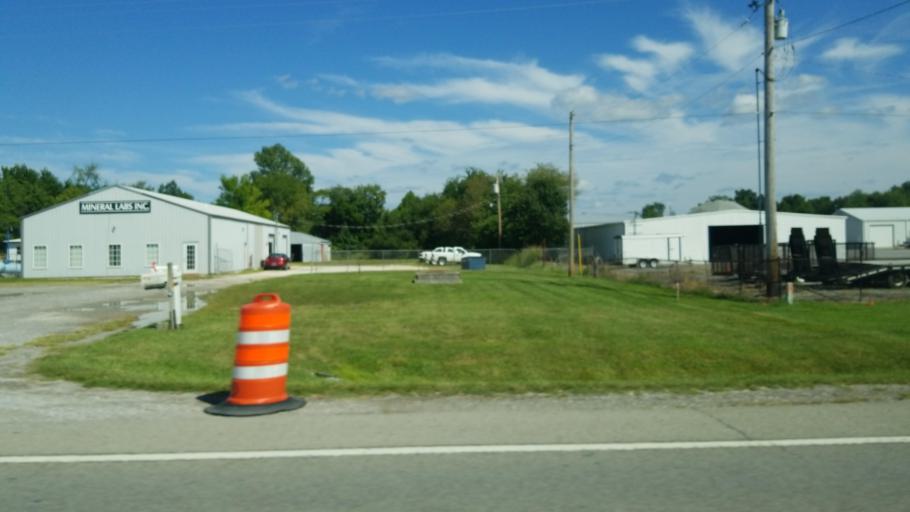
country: US
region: Illinois
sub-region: Williamson County
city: Marion
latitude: 37.7528
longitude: -88.9327
